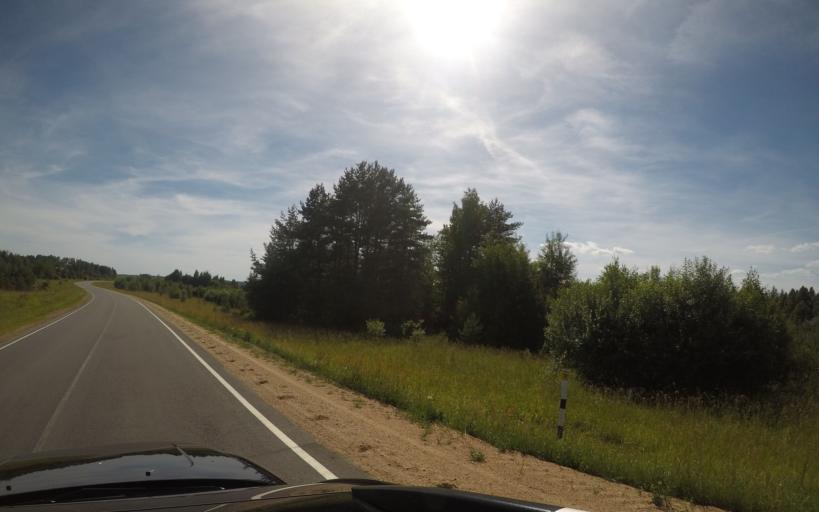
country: BY
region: Grodnenskaya
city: Hal'shany
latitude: 54.2717
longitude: 26.0320
